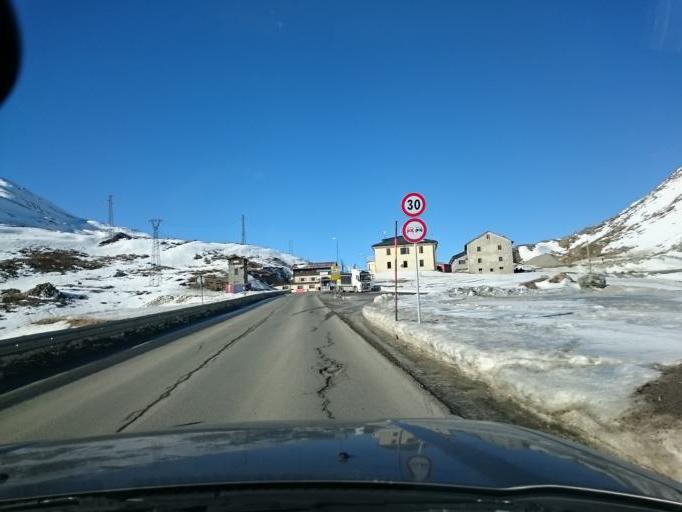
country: IT
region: Lombardy
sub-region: Provincia di Sondrio
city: Isolaccia
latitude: 46.4943
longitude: 10.2103
